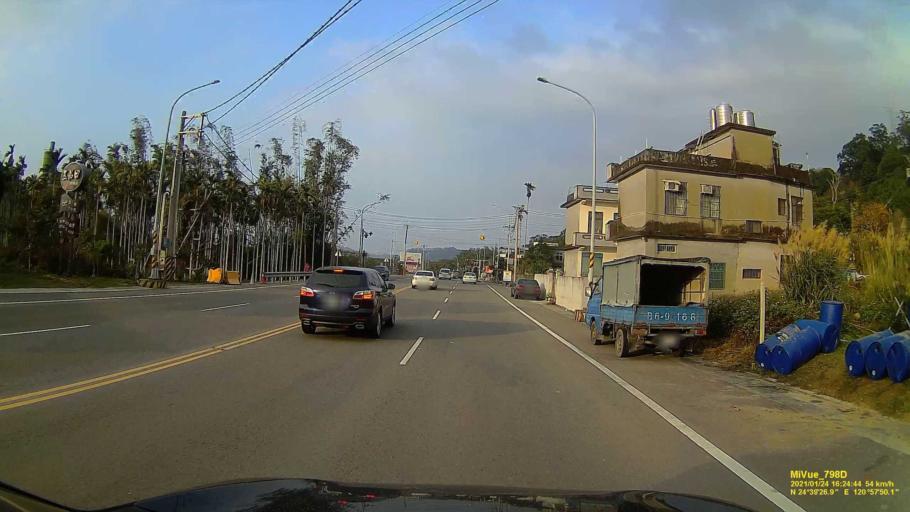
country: TW
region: Taiwan
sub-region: Hsinchu
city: Hsinchu
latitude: 24.6577
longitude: 120.9640
